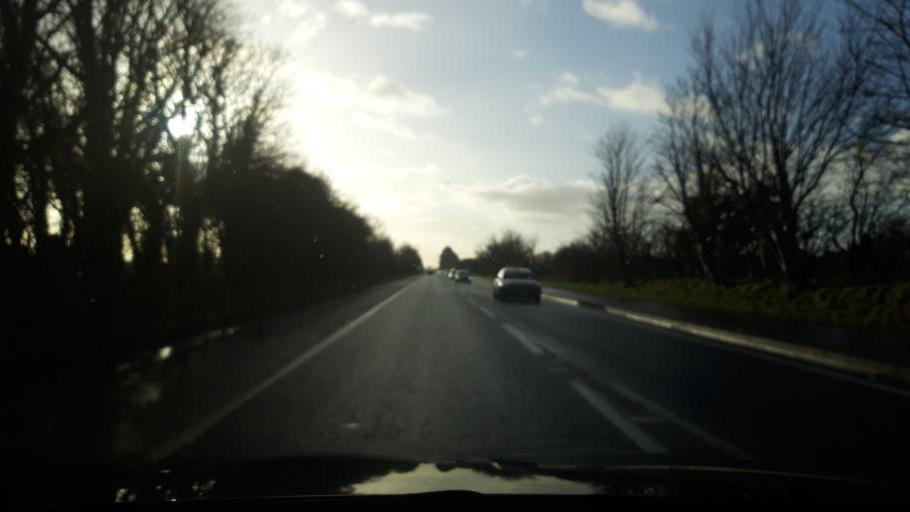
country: GB
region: Northern Ireland
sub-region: Coleraine District
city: Coleraine
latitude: 55.1140
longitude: -6.6873
